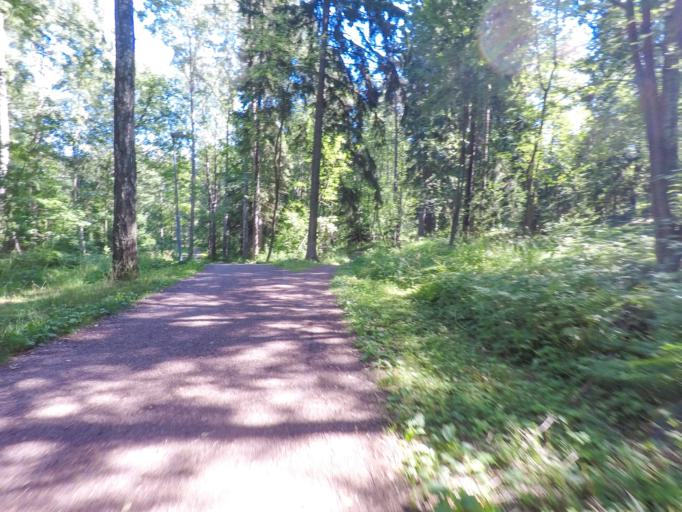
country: FI
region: Uusimaa
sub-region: Helsinki
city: Helsinki
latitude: 60.1794
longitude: 25.0429
